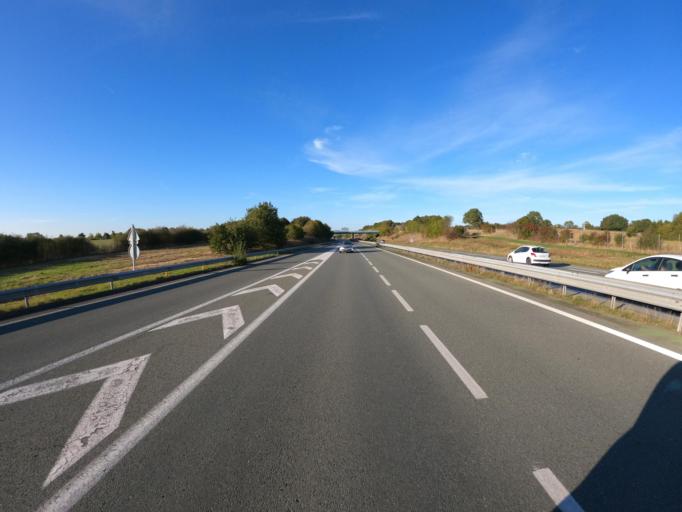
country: FR
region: Pays de la Loire
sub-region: Departement de Maine-et-Loire
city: Nuaille
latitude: 47.0884
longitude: -0.8240
